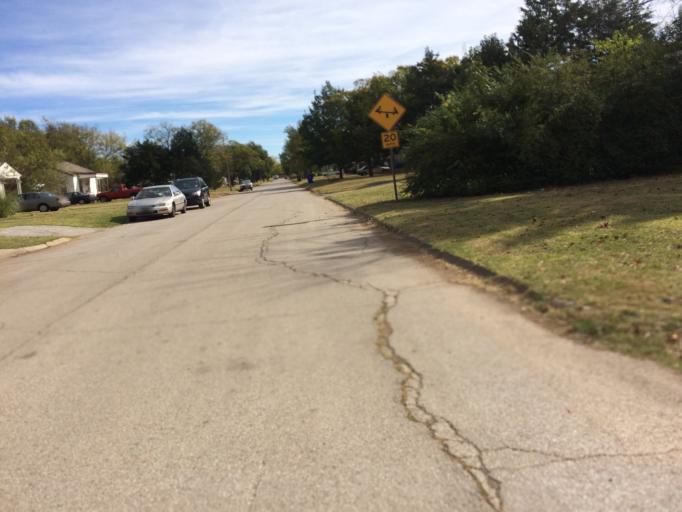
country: US
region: Oklahoma
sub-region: Cleveland County
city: Norman
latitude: 35.2334
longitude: -97.4476
